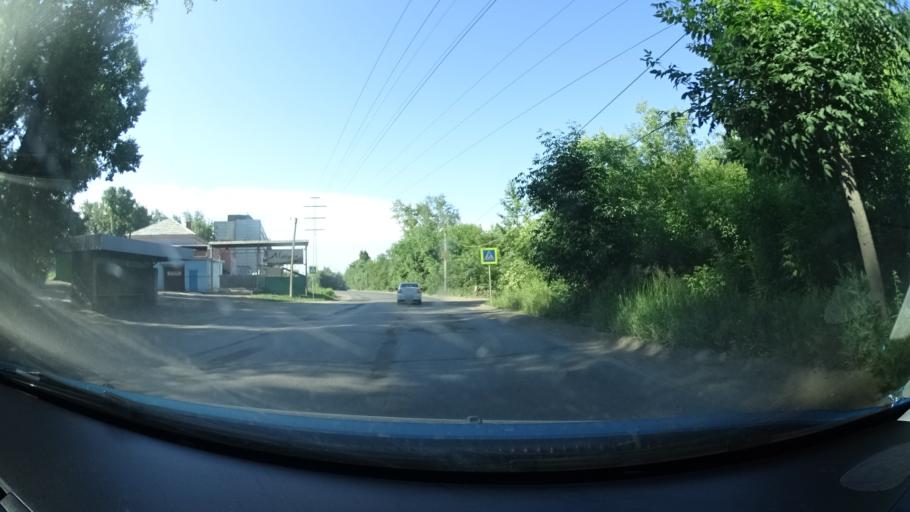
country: RU
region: Bashkortostan
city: Ufa
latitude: 54.8436
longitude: 56.0759
